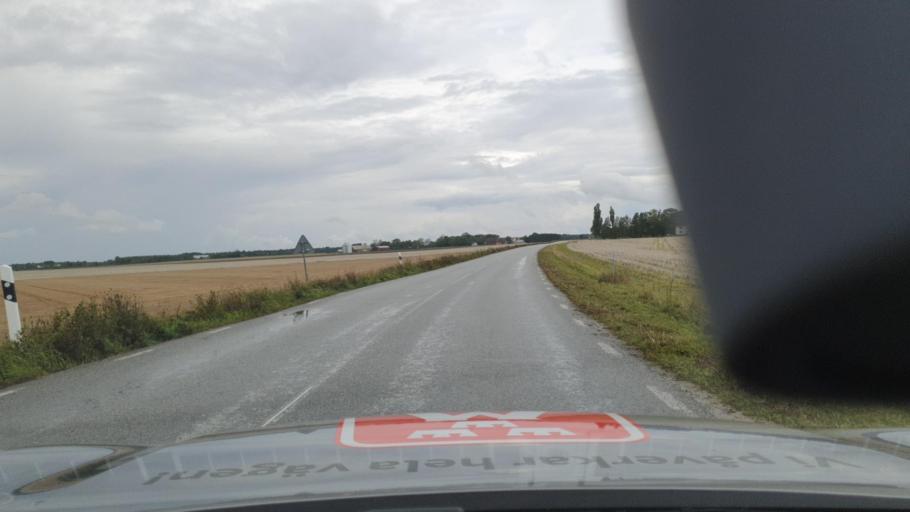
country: SE
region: Gotland
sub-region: Gotland
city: Visby
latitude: 57.5018
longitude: 18.4295
